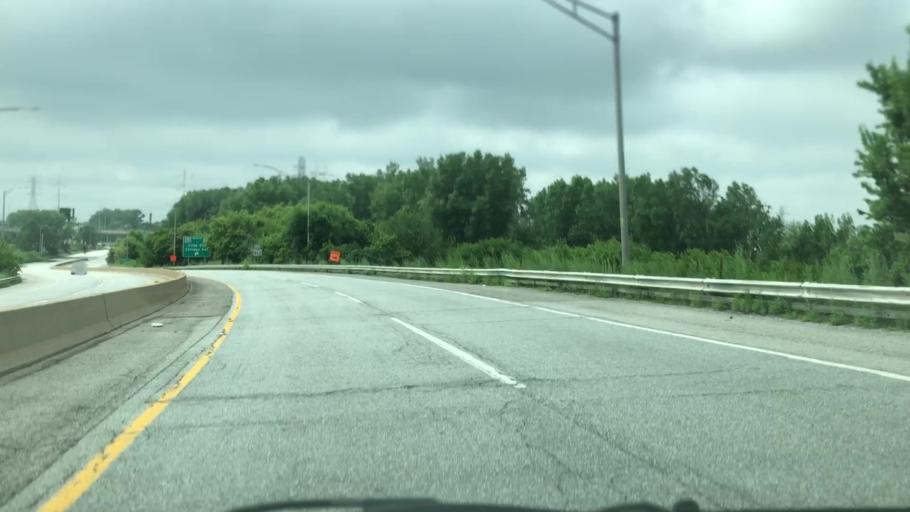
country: US
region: Indiana
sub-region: Lake County
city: East Chicago
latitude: 41.6178
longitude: -87.4264
